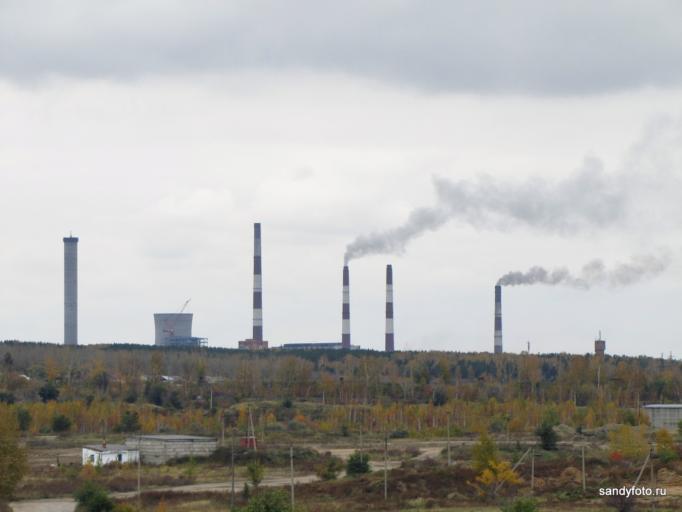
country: RU
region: Chelyabinsk
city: Troitsk
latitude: 54.0763
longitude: 61.6066
